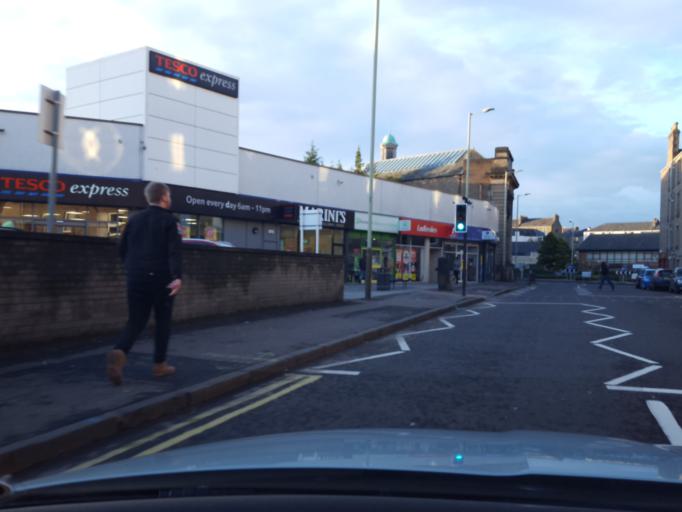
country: GB
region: Scotland
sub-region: Dundee City
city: Dundee
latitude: 56.4743
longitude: -2.9798
